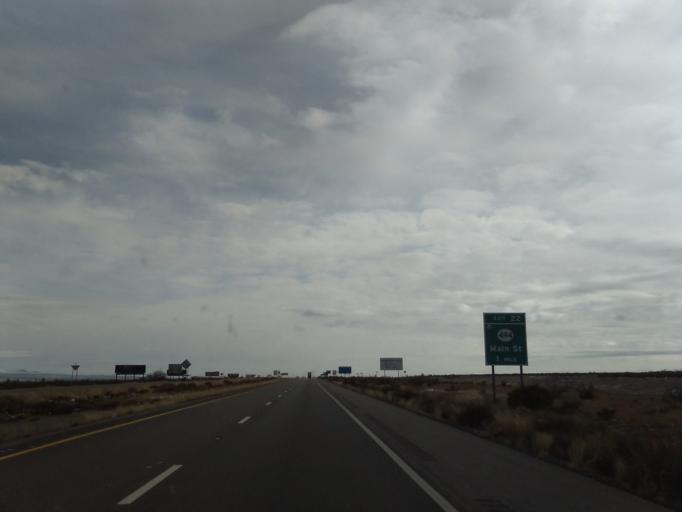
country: US
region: New Mexico
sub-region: Hidalgo County
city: Lordsburg
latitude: 32.3491
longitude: -108.7311
